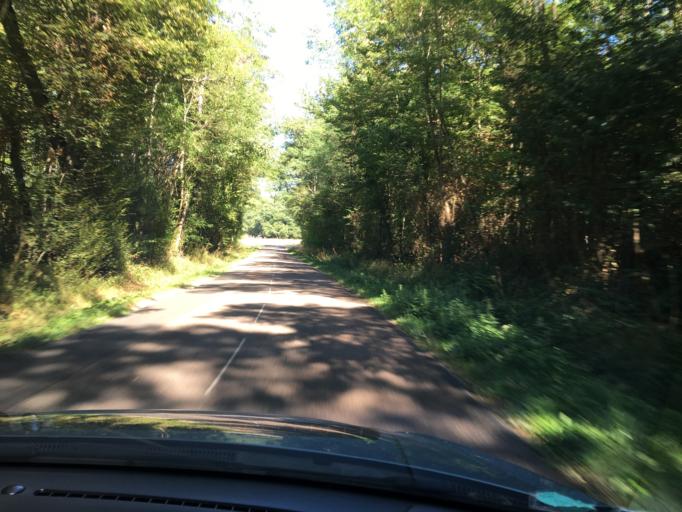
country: FR
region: Bourgogne
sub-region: Departement de l'Yonne
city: Appoigny
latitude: 47.8728
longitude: 3.5048
